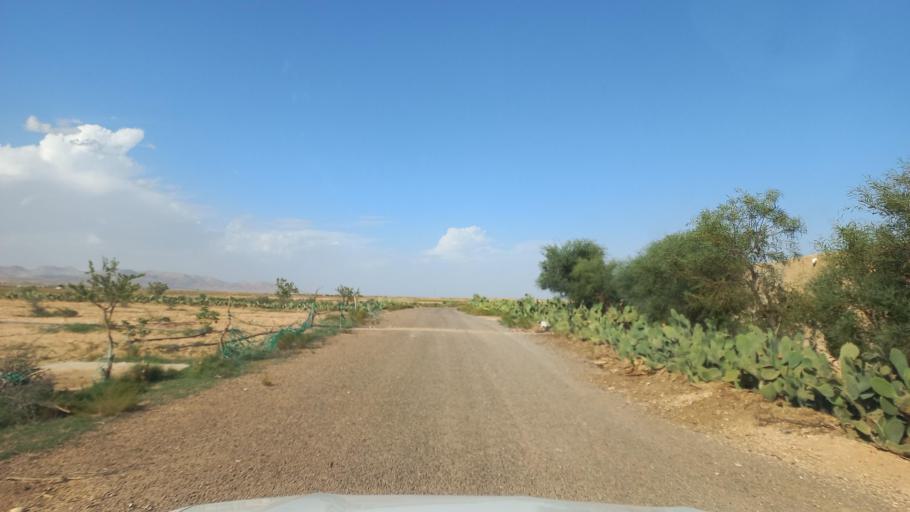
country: TN
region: Al Qasrayn
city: Kasserine
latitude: 35.3177
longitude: 9.0141
